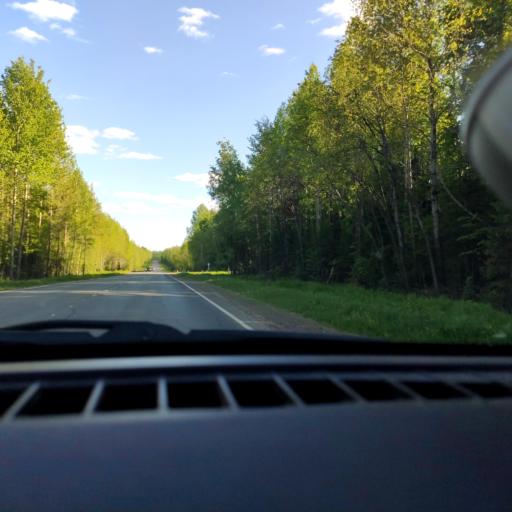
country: RU
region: Perm
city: Polazna
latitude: 58.2806
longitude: 56.1650
